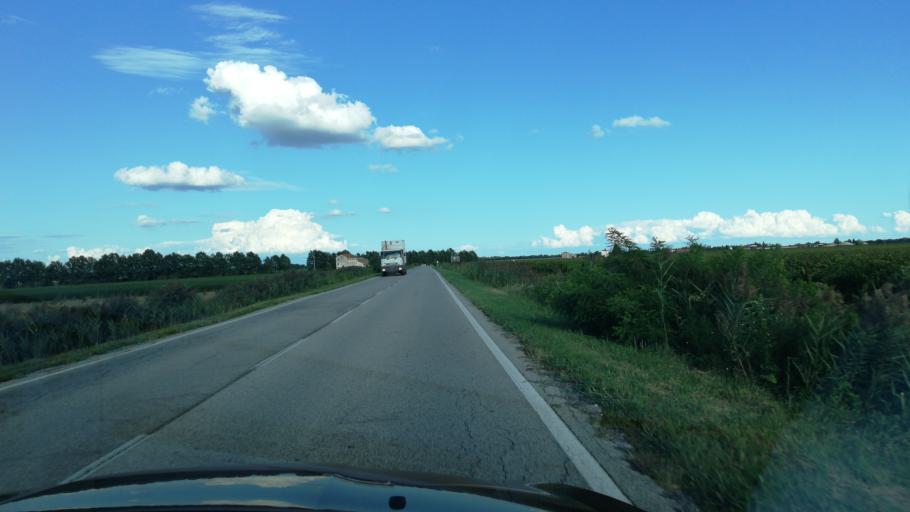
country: IT
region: Veneto
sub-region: Provincia di Venezia
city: San Giorgio di Livenza
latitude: 45.6356
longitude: 12.7575
